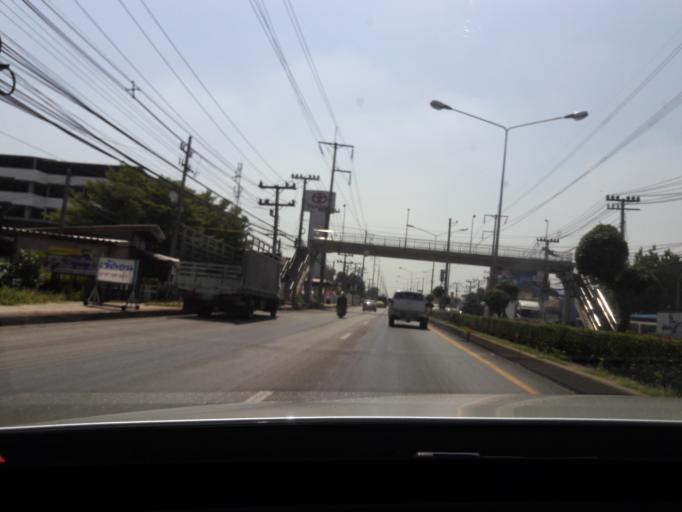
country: TH
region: Samut Sakhon
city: Krathum Baen
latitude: 13.6350
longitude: 100.2966
